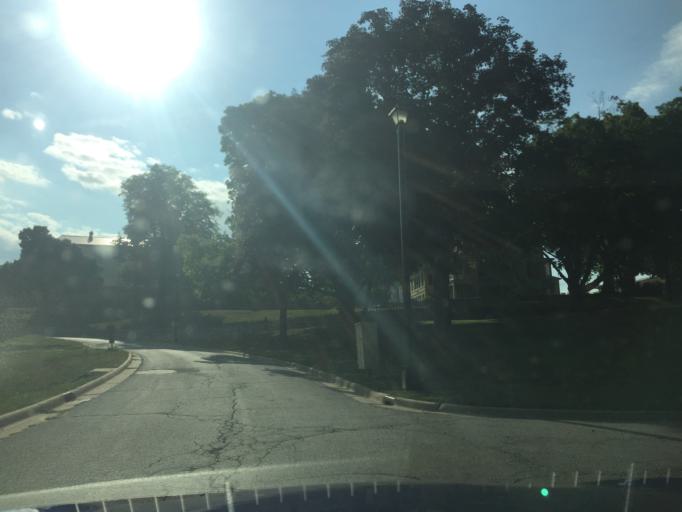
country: US
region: Kansas
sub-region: Leavenworth County
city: Leavenworth
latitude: 39.3580
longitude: -94.9152
